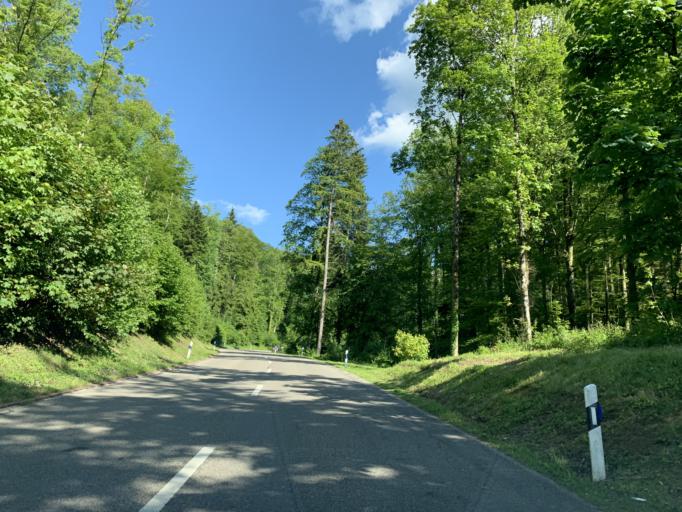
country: CH
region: Zurich
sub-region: Bezirk Pfaeffikon
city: Effretikon / Watt
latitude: 47.4420
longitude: 8.7066
